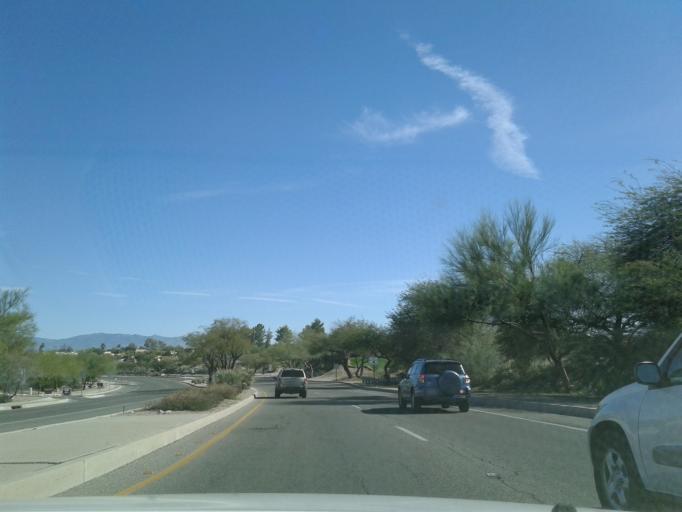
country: US
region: Arizona
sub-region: Pima County
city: Catalina Foothills
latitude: 32.3100
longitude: -110.9099
